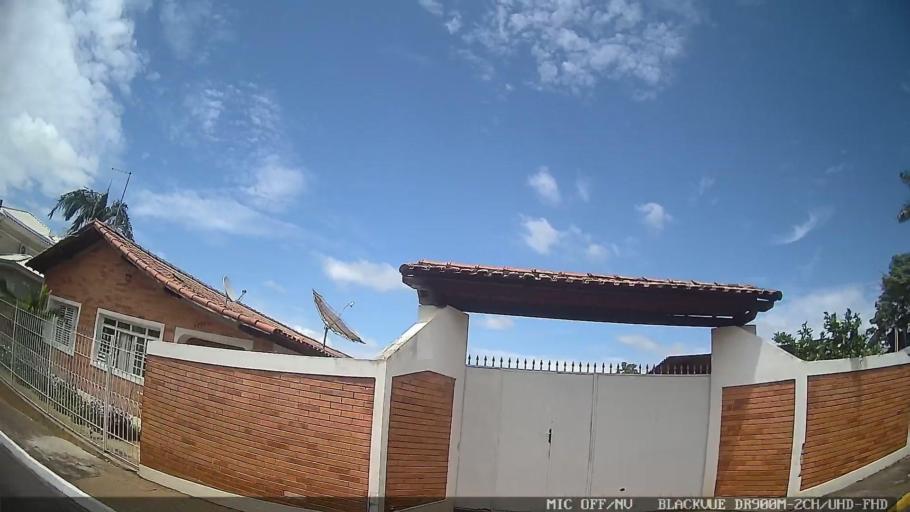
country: BR
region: Sao Paulo
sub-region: Laranjal Paulista
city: Laranjal Paulista
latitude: -23.0592
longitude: -47.8320
